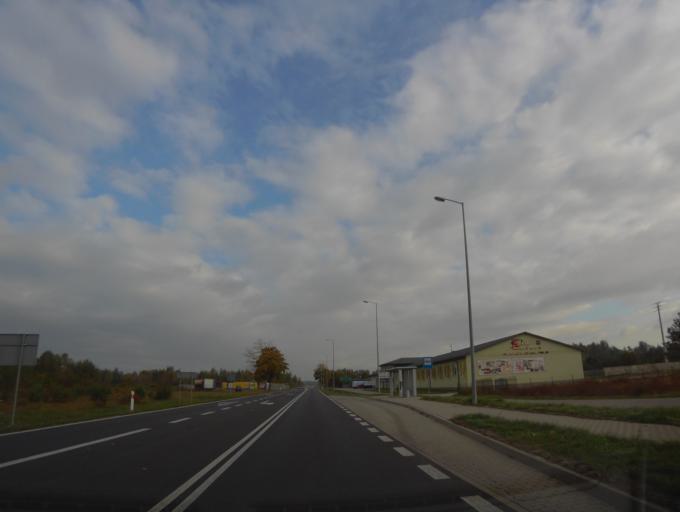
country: PL
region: Lublin Voivodeship
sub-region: Powiat bilgorajski
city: Frampol
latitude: 50.6273
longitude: 22.6846
